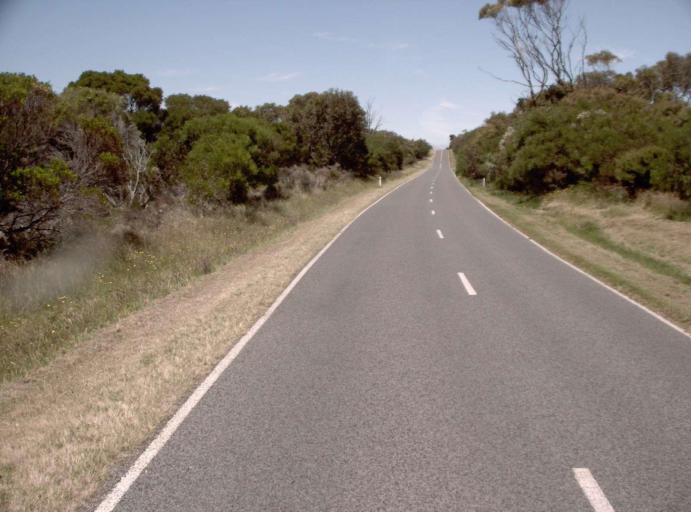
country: AU
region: Victoria
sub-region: Bass Coast
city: North Wonthaggi
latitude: -38.7613
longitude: 146.1506
